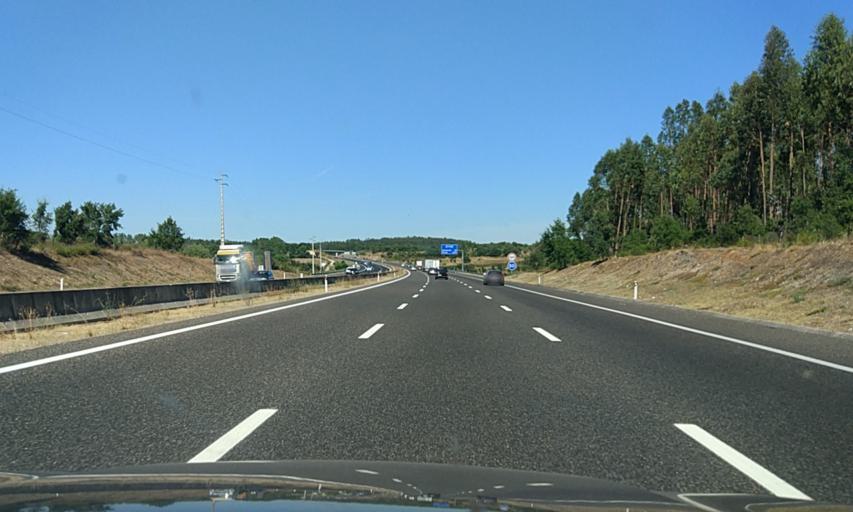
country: PT
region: Santarem
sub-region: Cartaxo
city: Cartaxo
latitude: 39.2098
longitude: -8.7855
